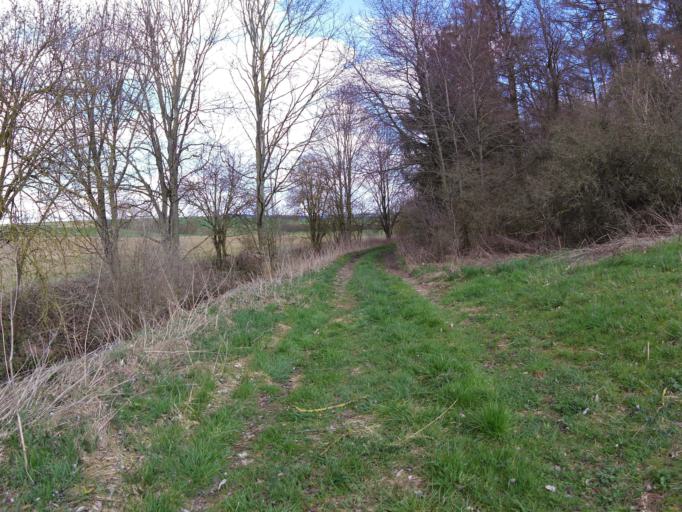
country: DE
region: Bavaria
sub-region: Regierungsbezirk Unterfranken
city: Biebelried
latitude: 49.7437
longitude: 10.0986
